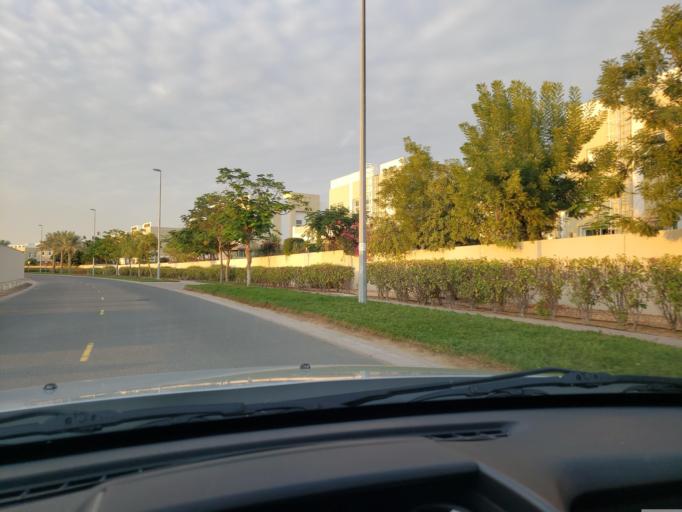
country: AE
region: Dubai
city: Dubai
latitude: 25.0204
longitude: 55.2706
